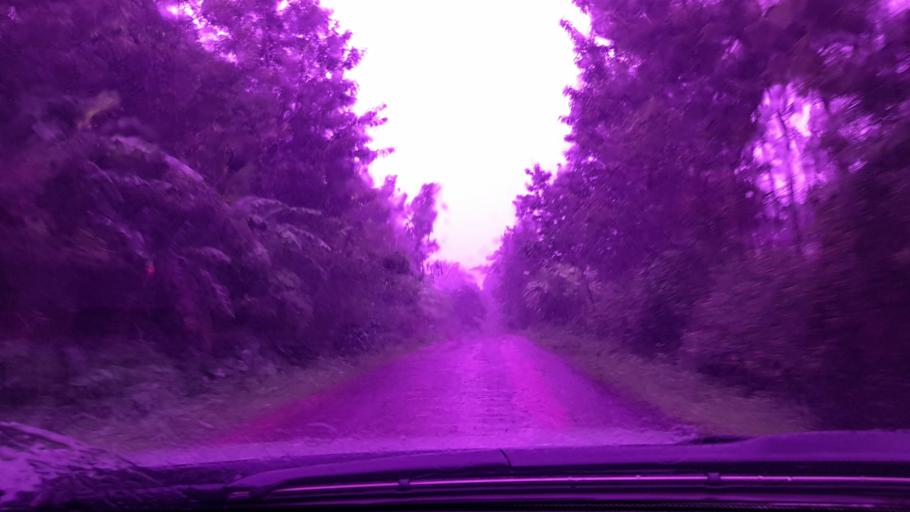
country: ET
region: Oromiya
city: Metu
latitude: 8.4666
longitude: 35.6397
